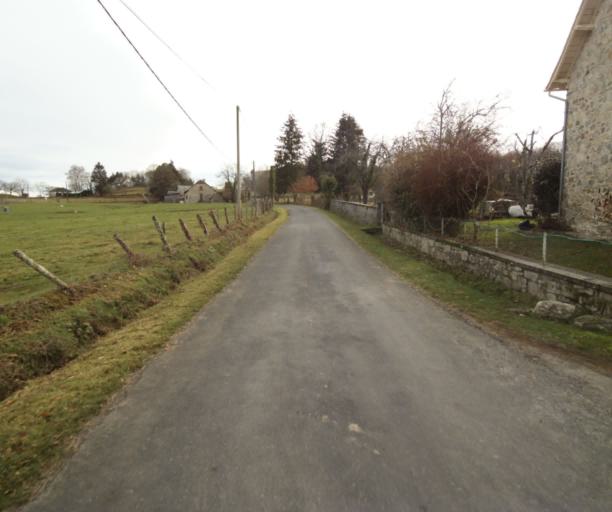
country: FR
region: Limousin
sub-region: Departement de la Correze
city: Saint-Mexant
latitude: 45.2807
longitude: 1.6782
